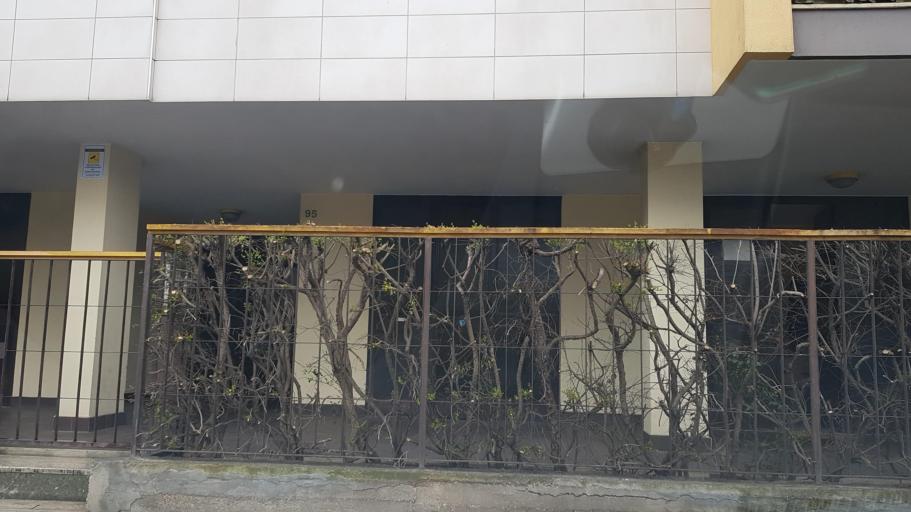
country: IT
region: Basilicate
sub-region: Provincia di Matera
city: Matera
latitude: 40.6781
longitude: 16.5869
